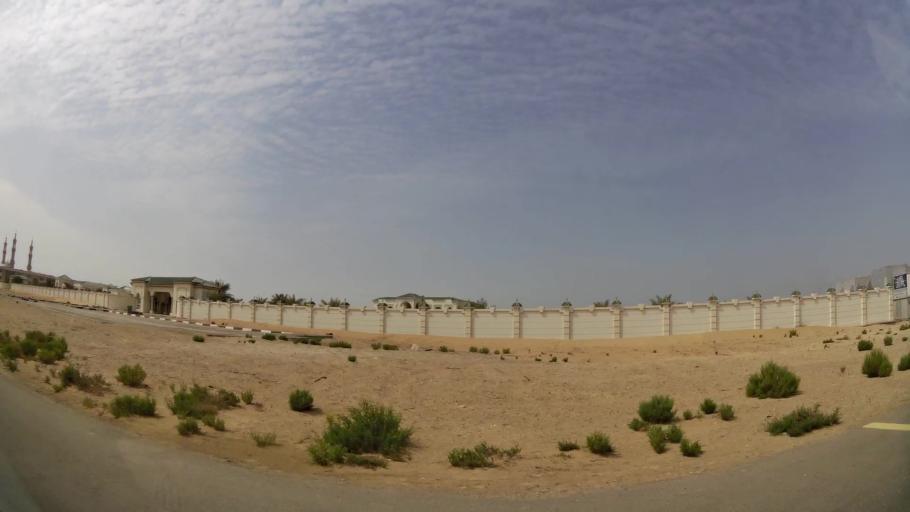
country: AE
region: Abu Dhabi
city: Abu Dhabi
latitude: 24.5190
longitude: 54.6688
